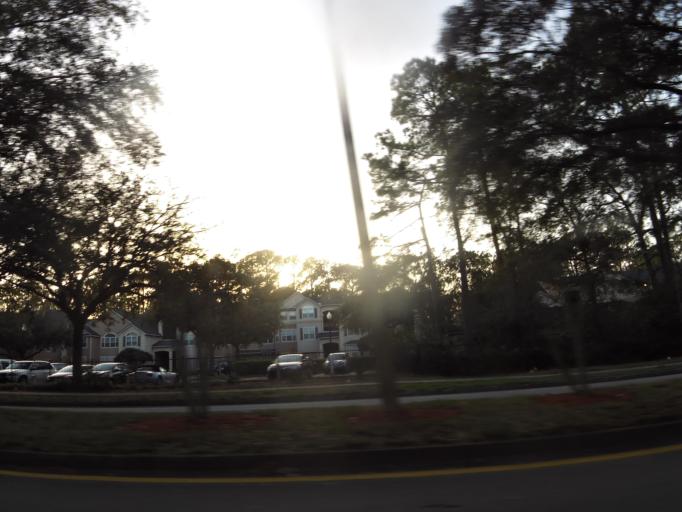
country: US
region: Florida
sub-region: Duval County
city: Jacksonville Beach
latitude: 30.2621
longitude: -81.4598
